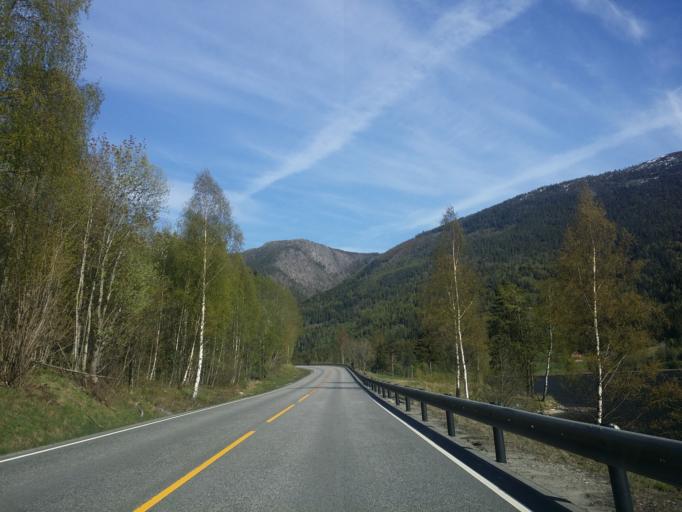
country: NO
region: Telemark
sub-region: Seljord
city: Seljord
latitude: 59.6101
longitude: 8.7546
